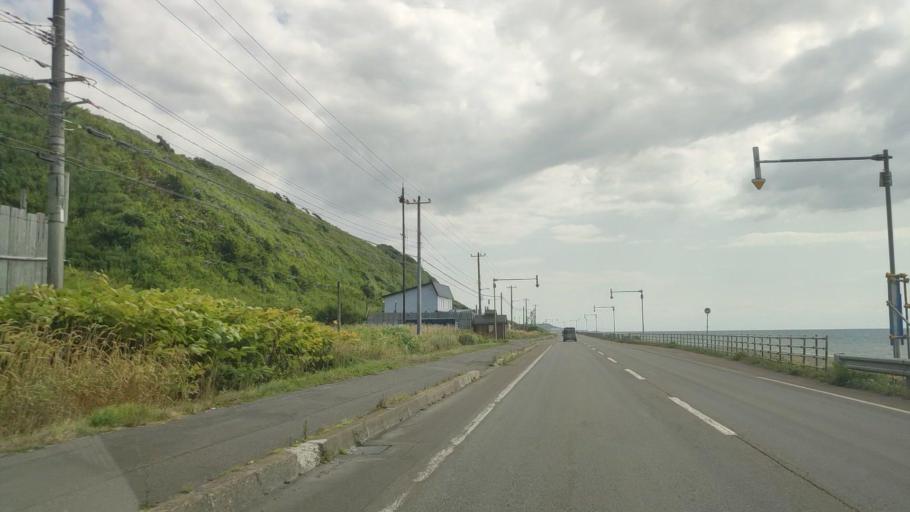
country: JP
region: Hokkaido
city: Rumoi
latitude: 44.1991
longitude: 141.6579
